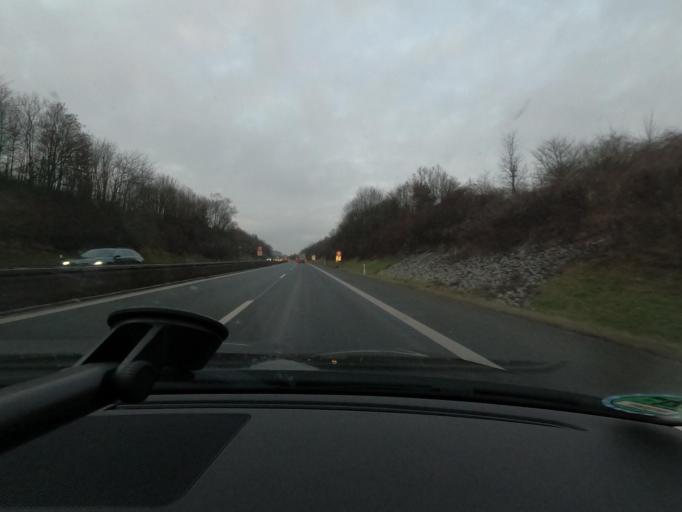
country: DE
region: Bavaria
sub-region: Upper Franconia
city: Hirschaid
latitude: 49.8361
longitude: 11.0047
